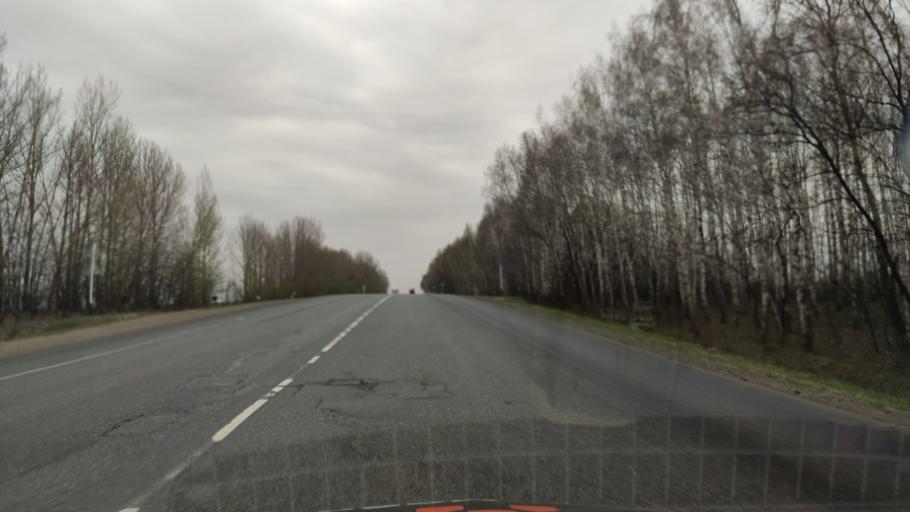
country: RU
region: Kursk
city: Gorshechnoye
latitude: 51.4810
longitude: 37.9575
